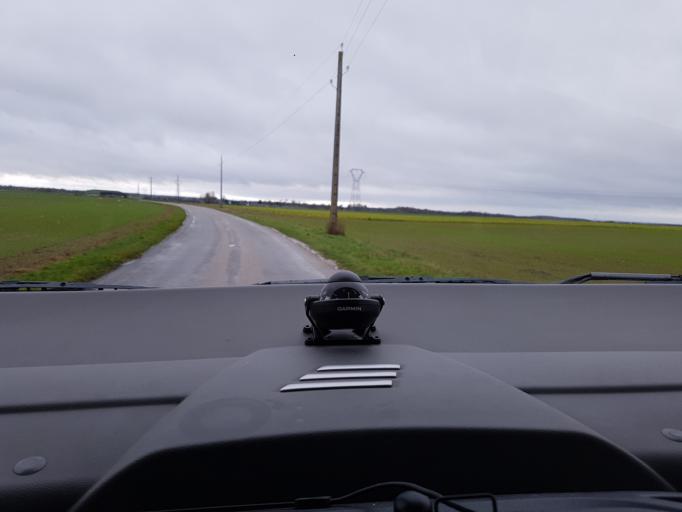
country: FR
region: Haute-Normandie
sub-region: Departement de l'Eure
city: Pont-Saint-Pierre
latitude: 49.2978
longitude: 1.3298
